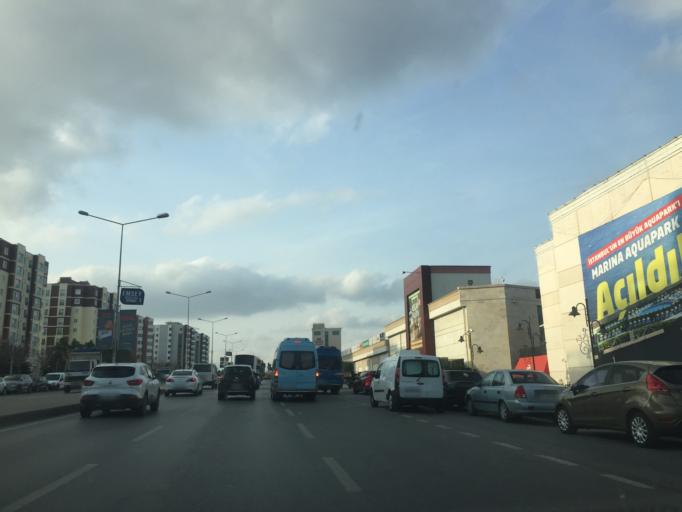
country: TR
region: Istanbul
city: Sultanbeyli
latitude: 40.9357
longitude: 29.3271
